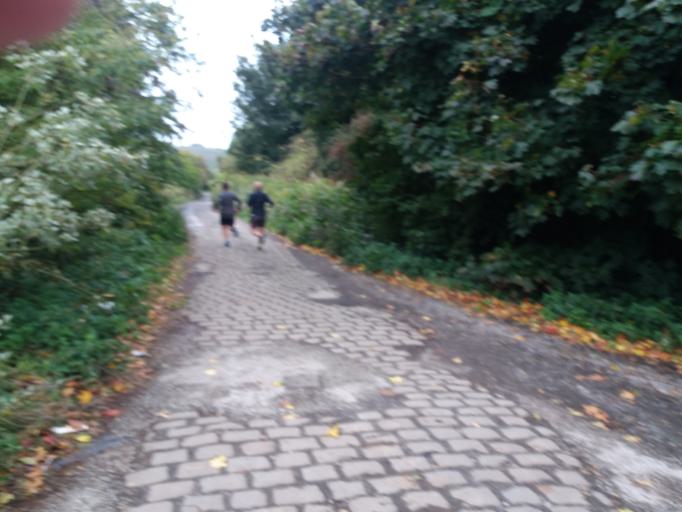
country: GB
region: England
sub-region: Lancashire
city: Chorley
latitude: 53.6652
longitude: -2.6157
